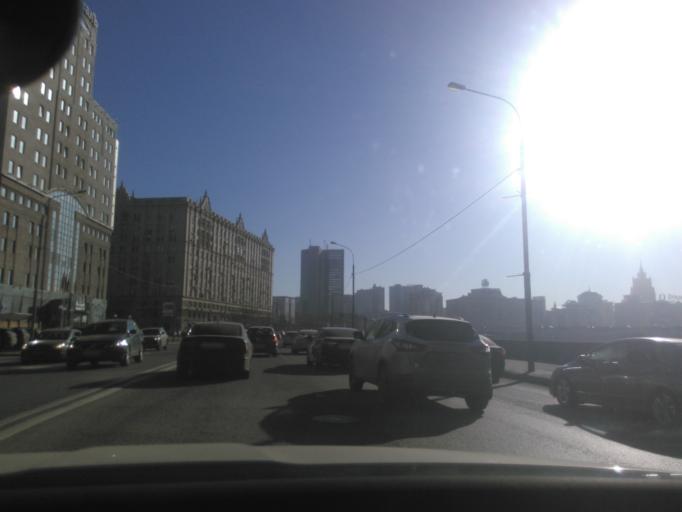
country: RU
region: Moskovskaya
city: Dorogomilovo
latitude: 55.7546
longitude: 37.5650
